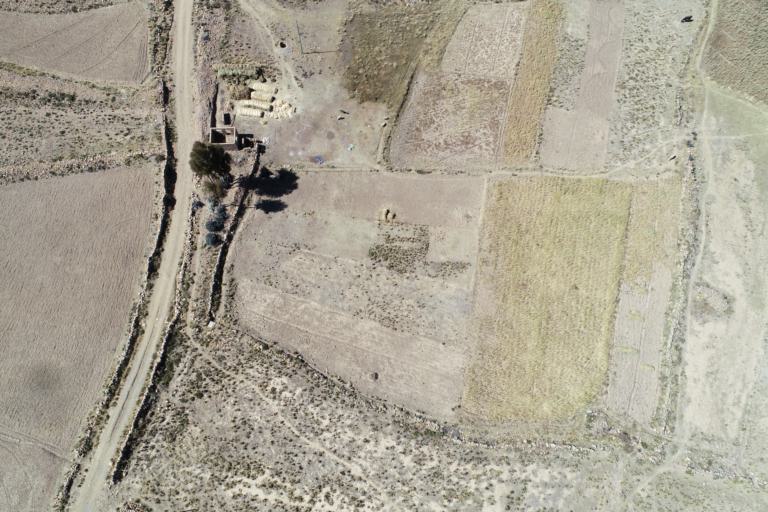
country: BO
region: La Paz
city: Achacachi
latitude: -15.8839
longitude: -68.8154
